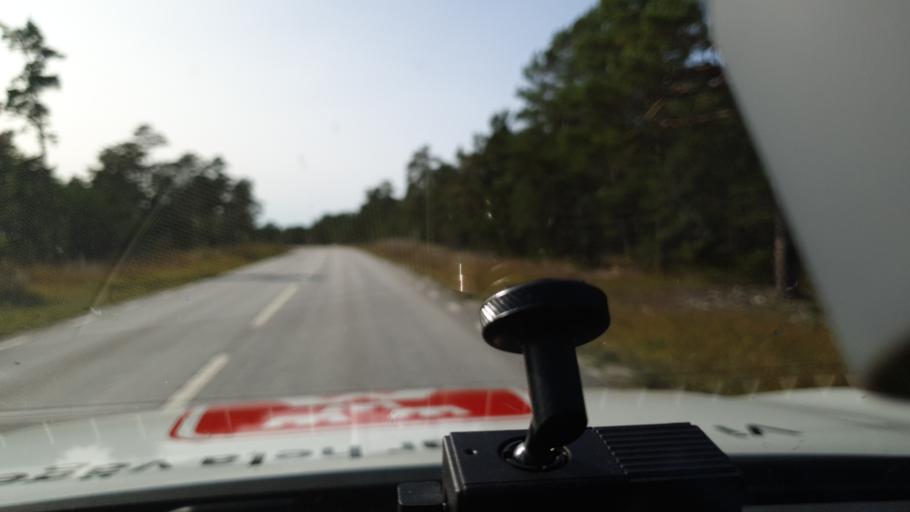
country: SE
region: Gotland
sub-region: Gotland
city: Slite
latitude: 57.8384
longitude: 18.9352
